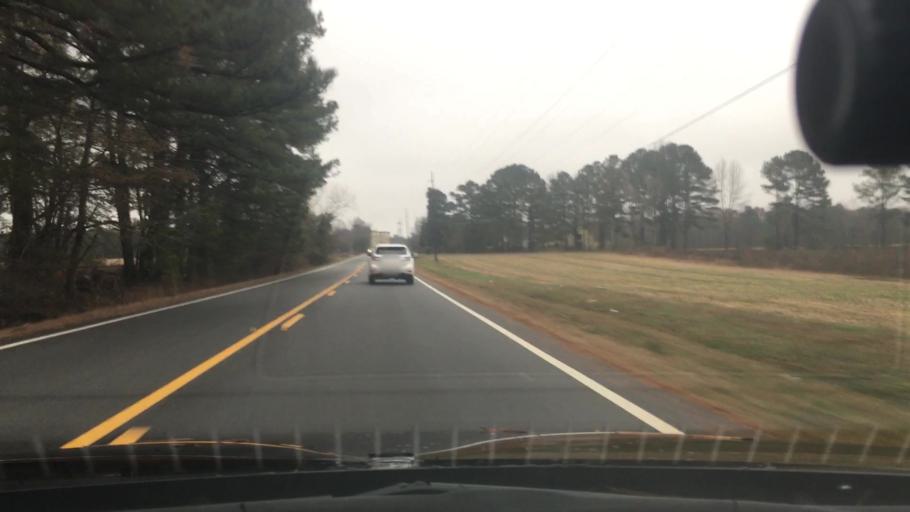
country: US
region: Georgia
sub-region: Coweta County
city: Senoia
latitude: 33.3107
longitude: -84.6054
